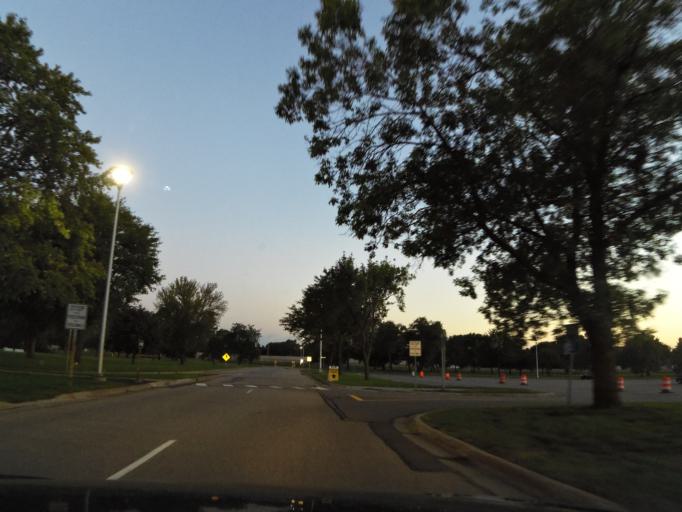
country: US
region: Minnesota
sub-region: Ramsey County
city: Maplewood
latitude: 44.9512
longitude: -92.9911
